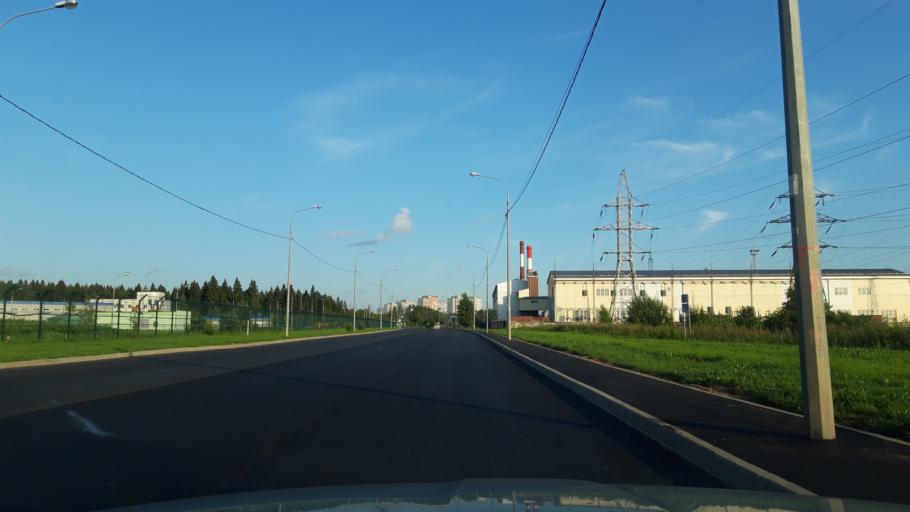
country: RU
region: Moskovskaya
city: Alabushevo
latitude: 56.0000
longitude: 37.1558
